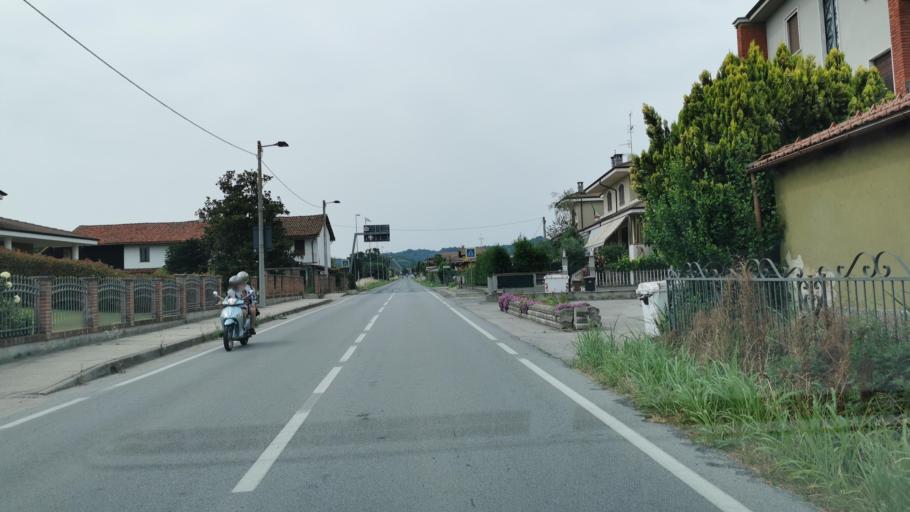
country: IT
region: Piedmont
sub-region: Provincia di Cuneo
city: Pocapaglia
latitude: 44.6904
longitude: 7.8930
